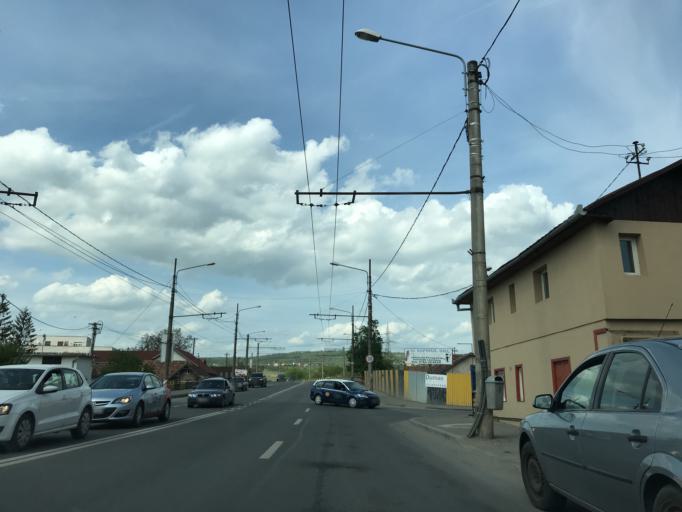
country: RO
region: Cluj
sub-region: Municipiul Cluj-Napoca
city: Cluj-Napoca
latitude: 46.7892
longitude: 23.6156
